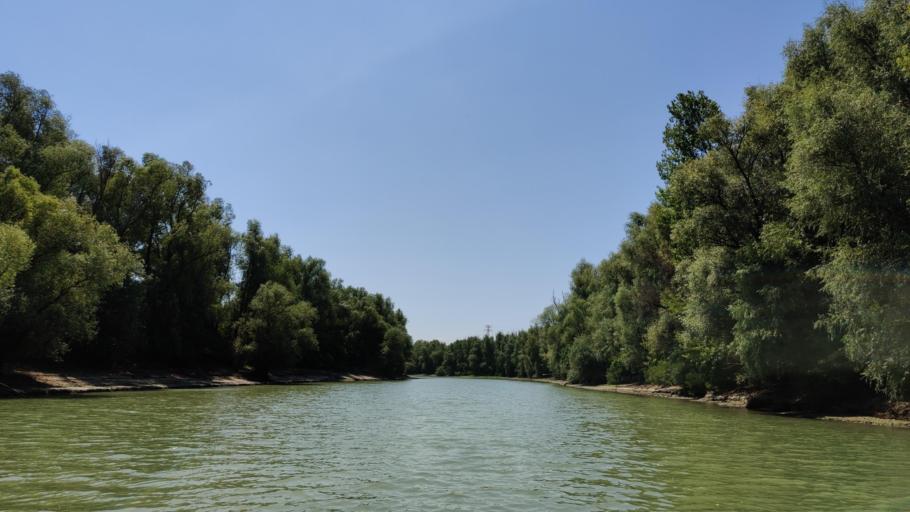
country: RO
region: Tulcea
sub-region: Municipiul Tulcea
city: Tulcea
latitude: 45.2083
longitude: 28.8558
